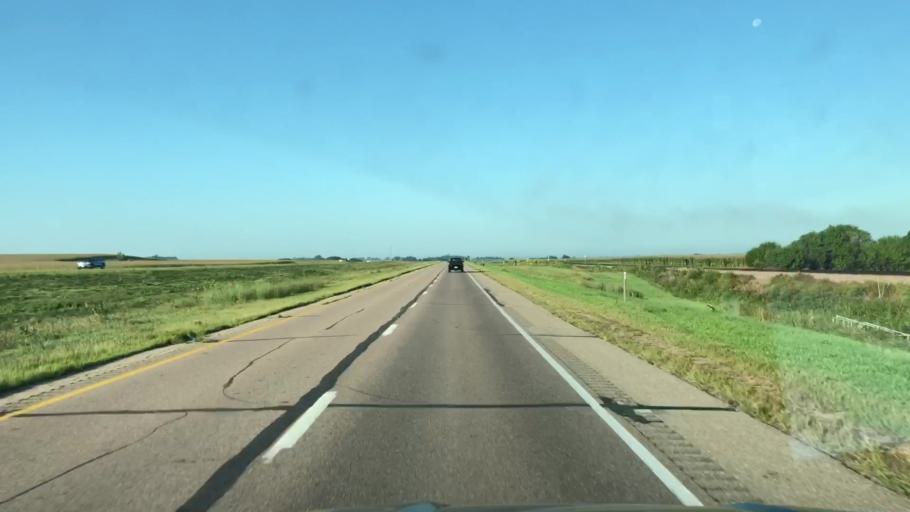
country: US
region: Iowa
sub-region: Sioux County
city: Alton
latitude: 43.0232
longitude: -95.9476
